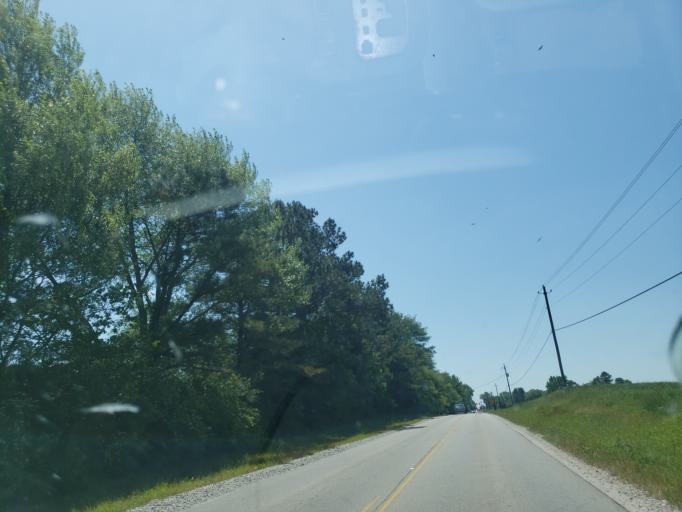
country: US
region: Alabama
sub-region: Madison County
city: Harvest
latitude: 34.8879
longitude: -86.7377
